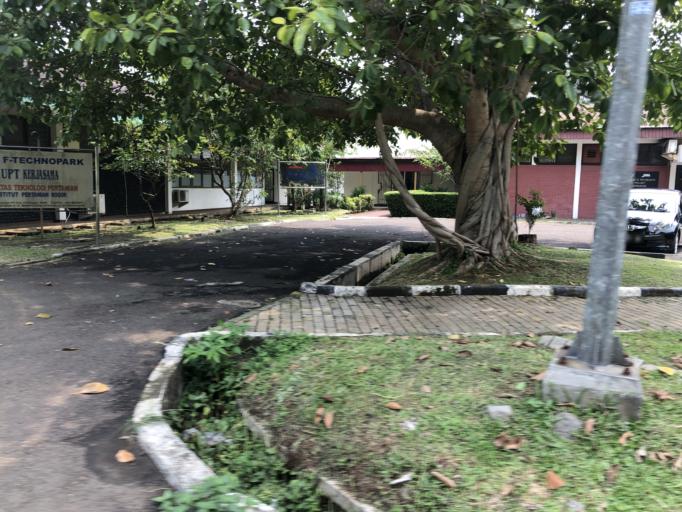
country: ID
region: West Java
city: Ciampea
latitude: -6.5572
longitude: 106.7267
